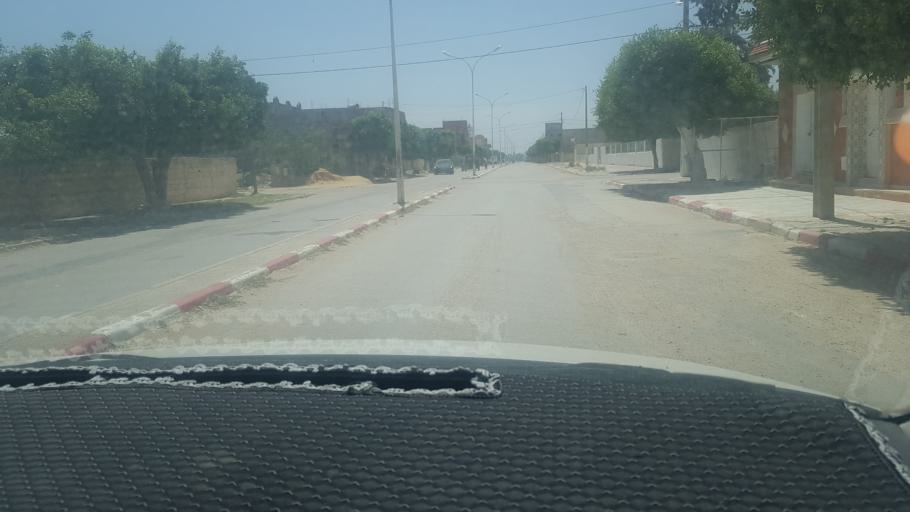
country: TN
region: Al Qayrawan
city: Kairouan
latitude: 35.6194
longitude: 9.9267
